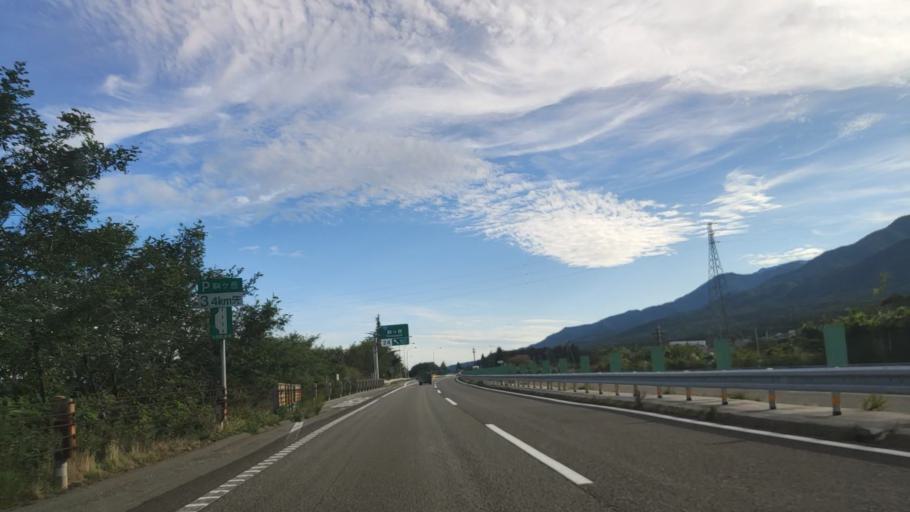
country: JP
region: Nagano
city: Ina
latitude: 35.7454
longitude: 137.9118
